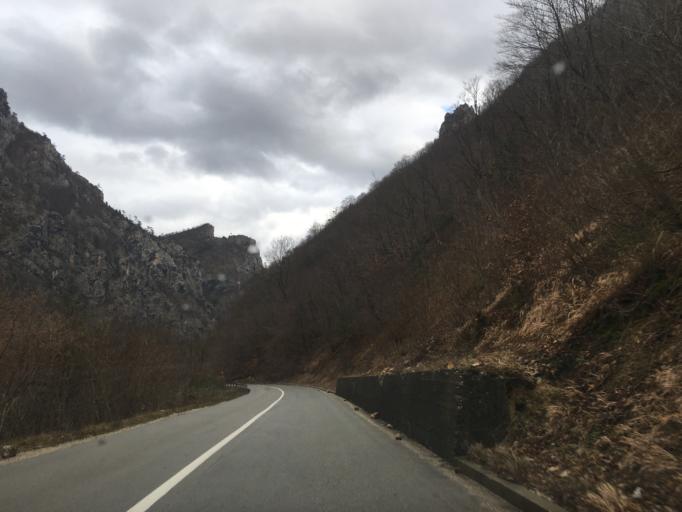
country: RS
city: Sokolovo Brdo
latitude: 43.1809
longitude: 19.7650
